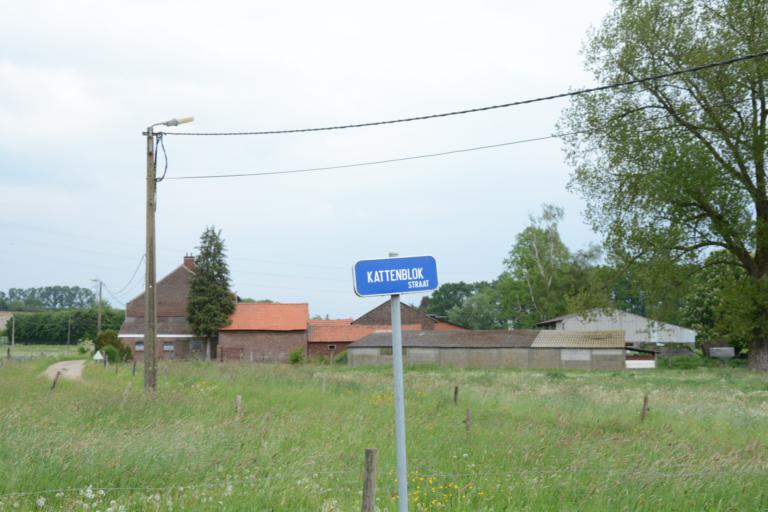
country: BE
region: Flanders
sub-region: Provincie Vlaams-Brabant
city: Lubbeek
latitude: 50.8627
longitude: 4.8121
